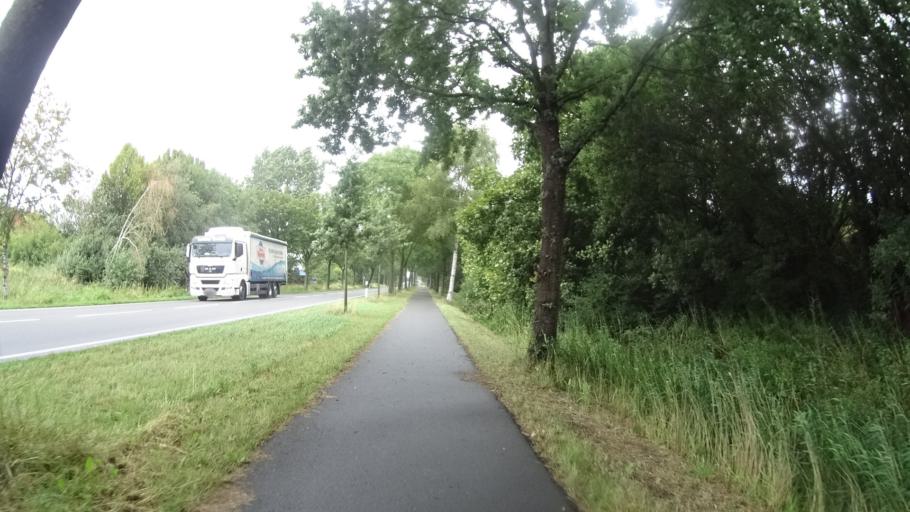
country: DE
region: Lower Saxony
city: Leer
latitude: 53.2221
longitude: 7.4364
